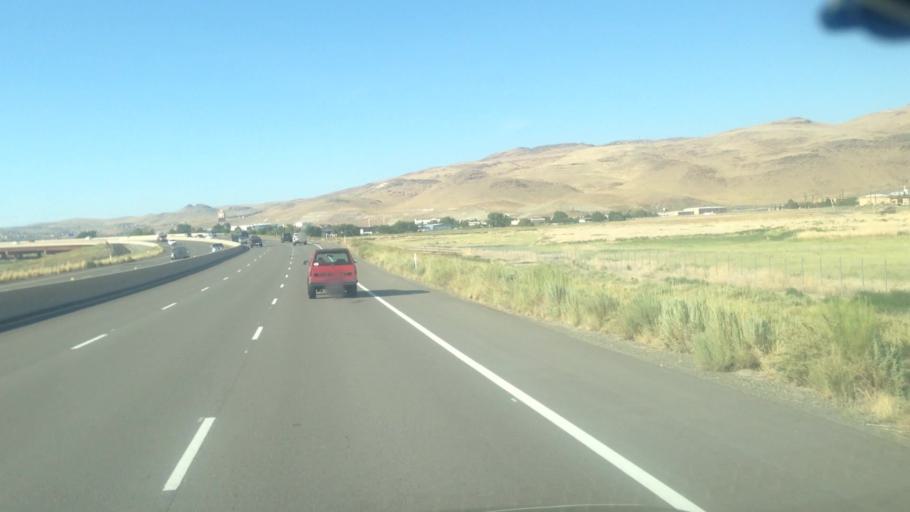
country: US
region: Nevada
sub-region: Washoe County
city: Sparks
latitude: 39.5143
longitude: -119.7123
